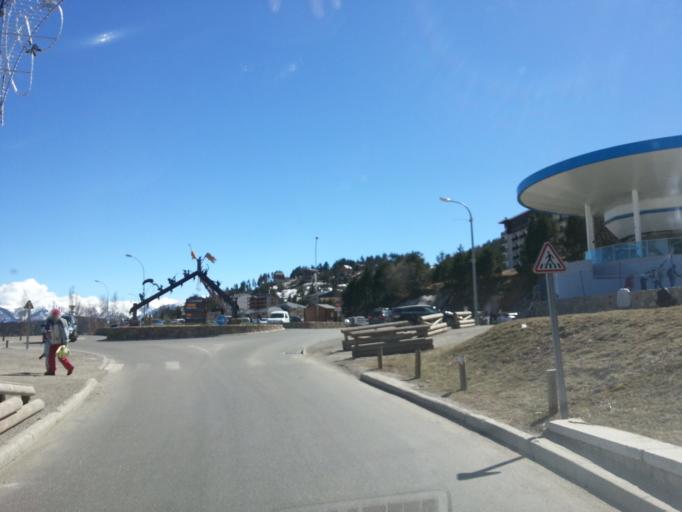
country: ES
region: Catalonia
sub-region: Provincia de Girona
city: Llivia
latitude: 42.5754
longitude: 2.0693
